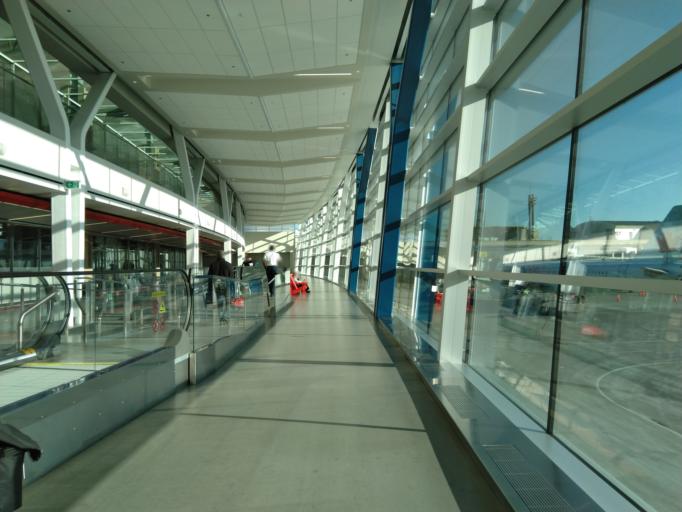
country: CA
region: Alberta
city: Calgary
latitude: 51.1302
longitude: -114.0099
